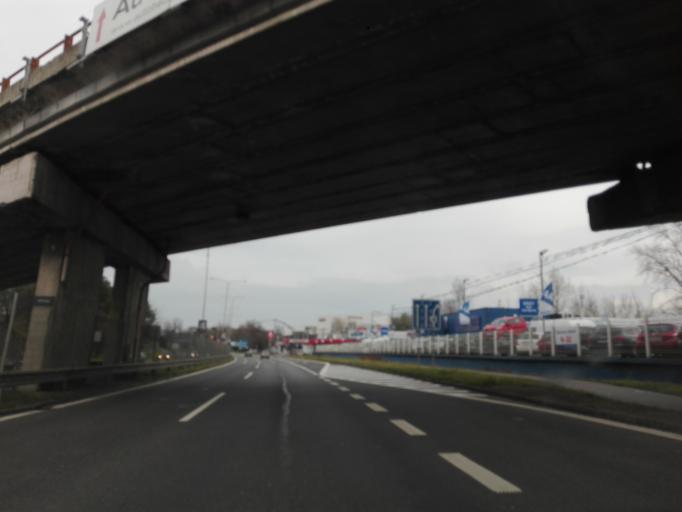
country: CZ
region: Moravskoslezsky
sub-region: Okres Ostrava-Mesto
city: Ostrava
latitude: 49.8260
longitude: 18.2805
